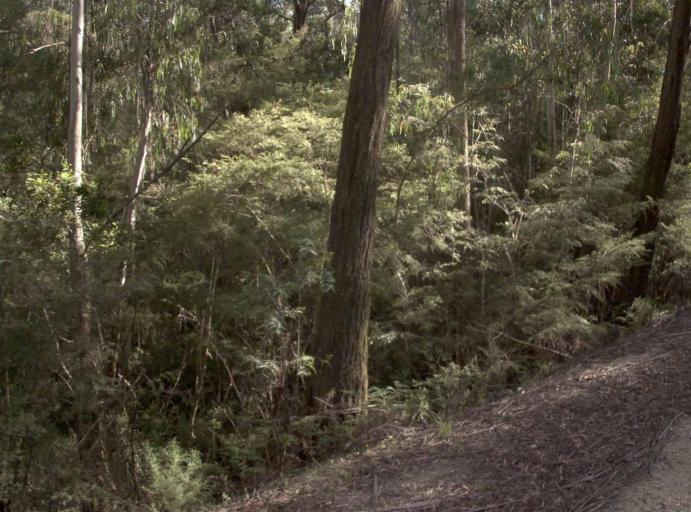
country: AU
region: Victoria
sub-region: East Gippsland
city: Lakes Entrance
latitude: -37.6663
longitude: 148.0695
